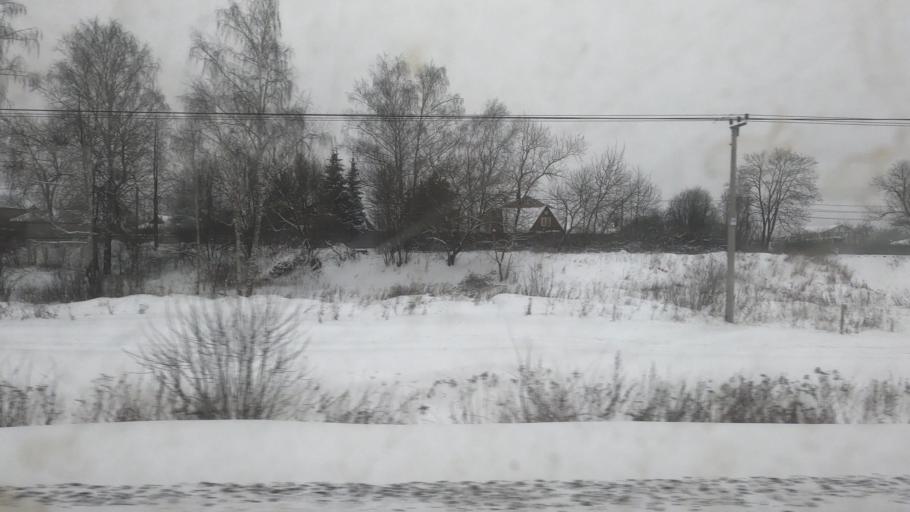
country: RU
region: Moskovskaya
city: Chornaya
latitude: 55.7529
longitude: 38.0453
